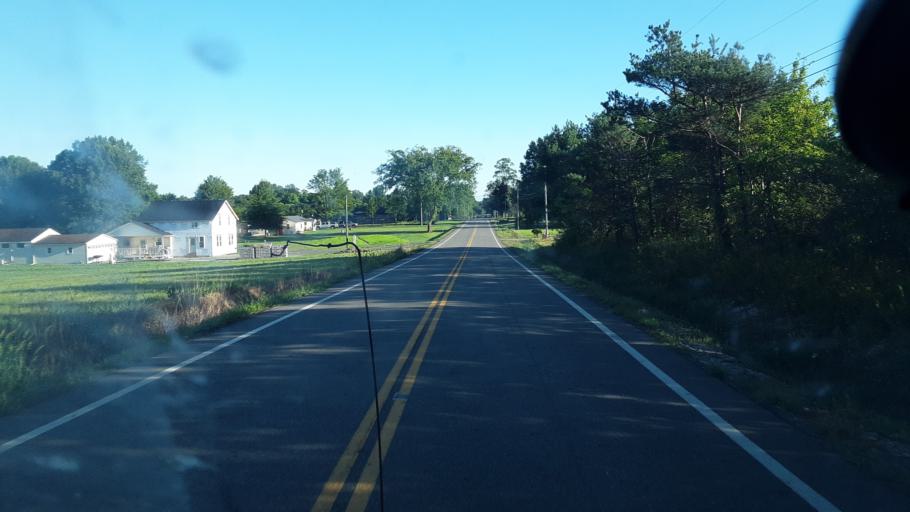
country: US
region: Ohio
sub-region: Trumbull County
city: Leavittsburg
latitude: 41.3176
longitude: -80.9561
